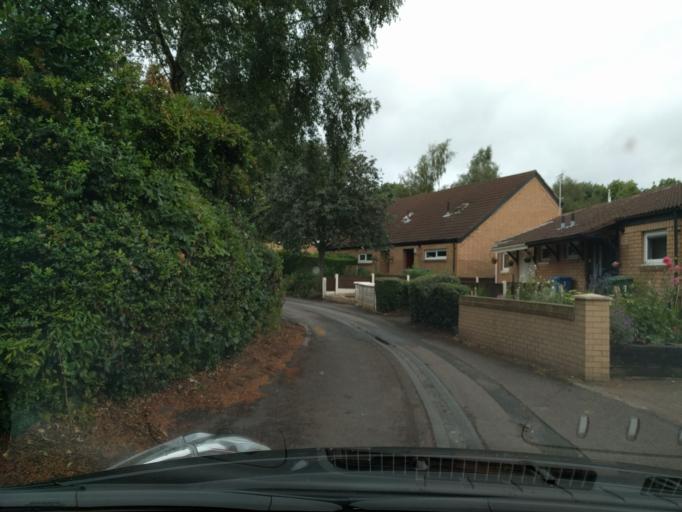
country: GB
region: England
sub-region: Warrington
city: Croft
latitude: 53.4203
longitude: -2.5222
